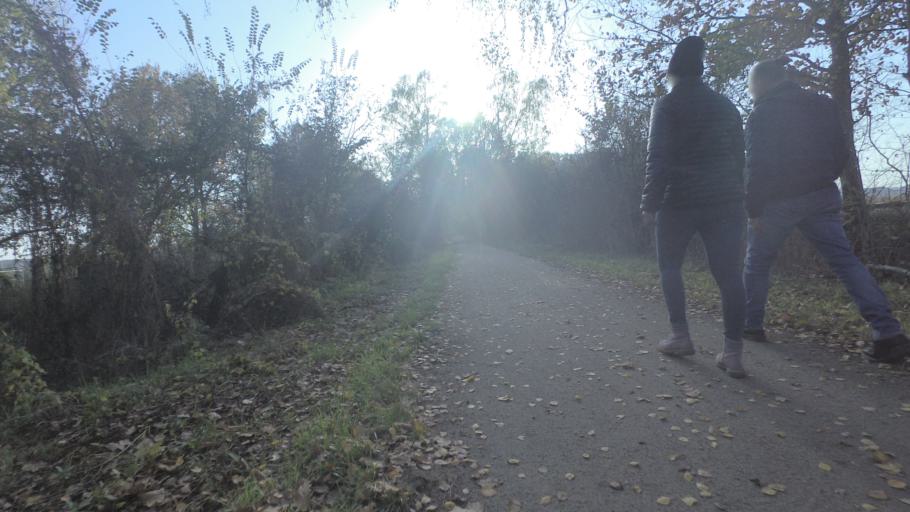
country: DE
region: Brandenburg
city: Am Mellensee
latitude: 52.1971
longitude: 13.4135
